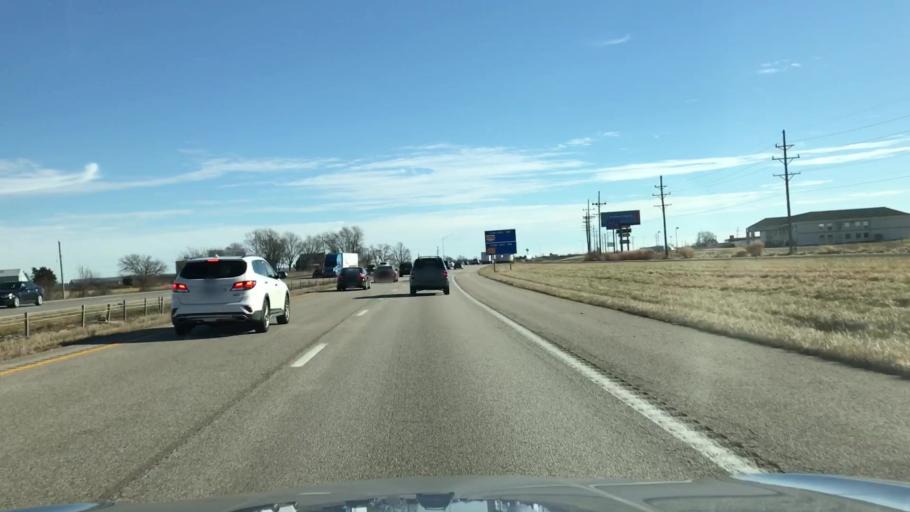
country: US
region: Missouri
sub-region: Warren County
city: Warrenton
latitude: 38.8440
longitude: -91.2318
